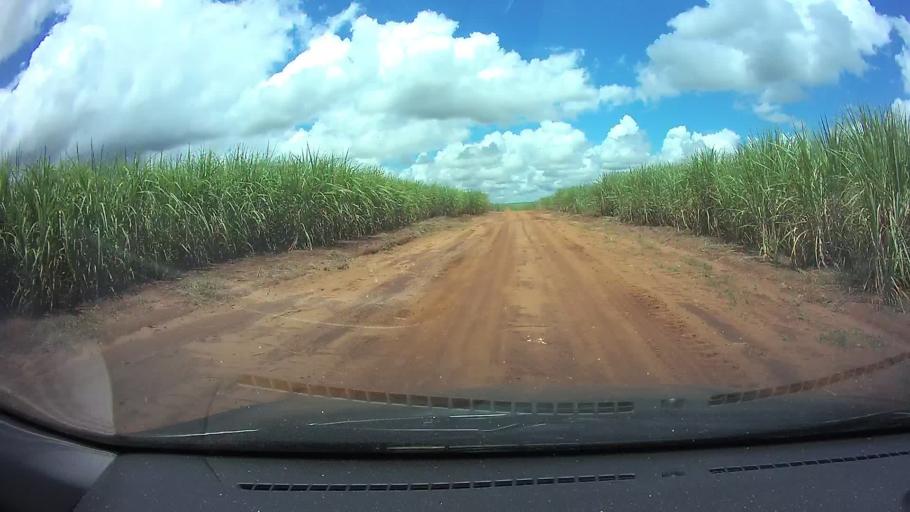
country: PY
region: Paraguari
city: La Colmena
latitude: -25.9533
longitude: -56.7667
